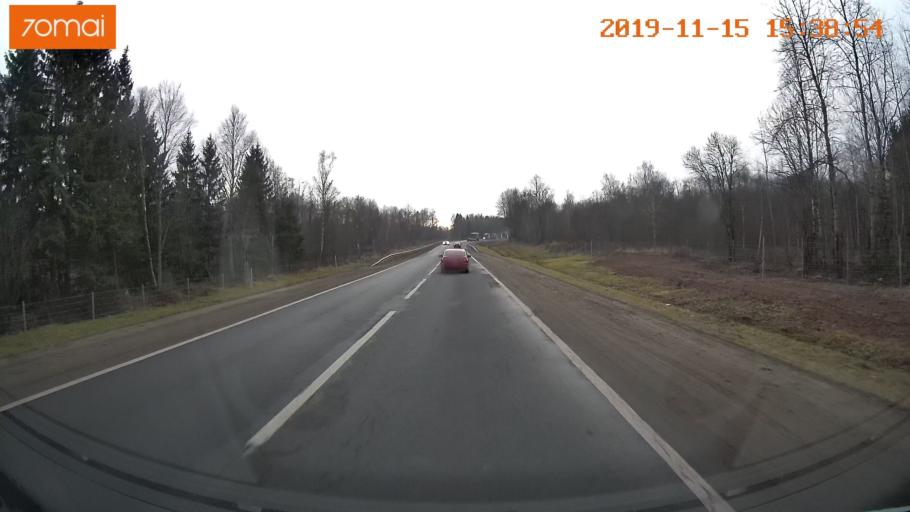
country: RU
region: Jaroslavl
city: Danilov
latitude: 58.0257
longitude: 40.0750
